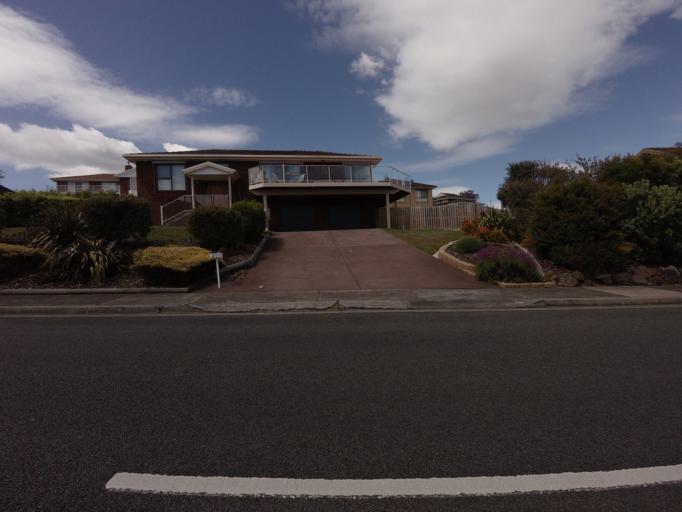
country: AU
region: Tasmania
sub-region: Clarence
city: Howrah
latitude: -42.8878
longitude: 147.4108
